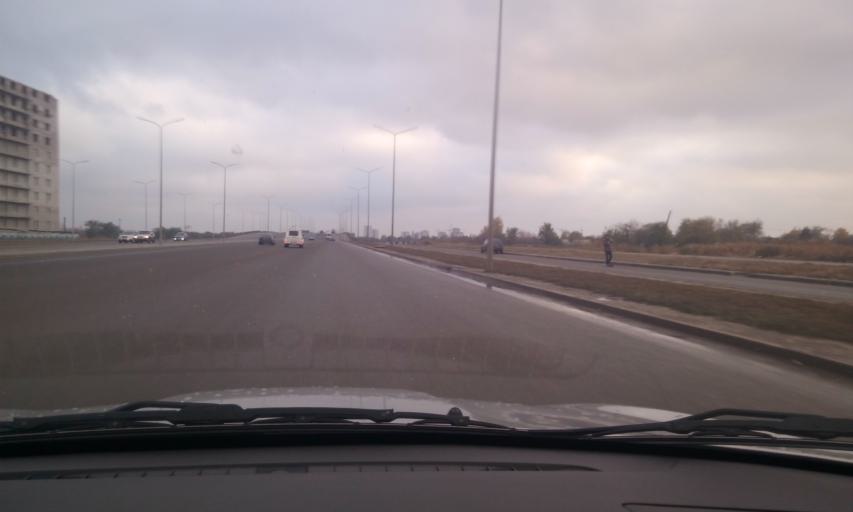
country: KZ
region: Astana Qalasy
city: Astana
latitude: 51.1691
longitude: 71.3759
